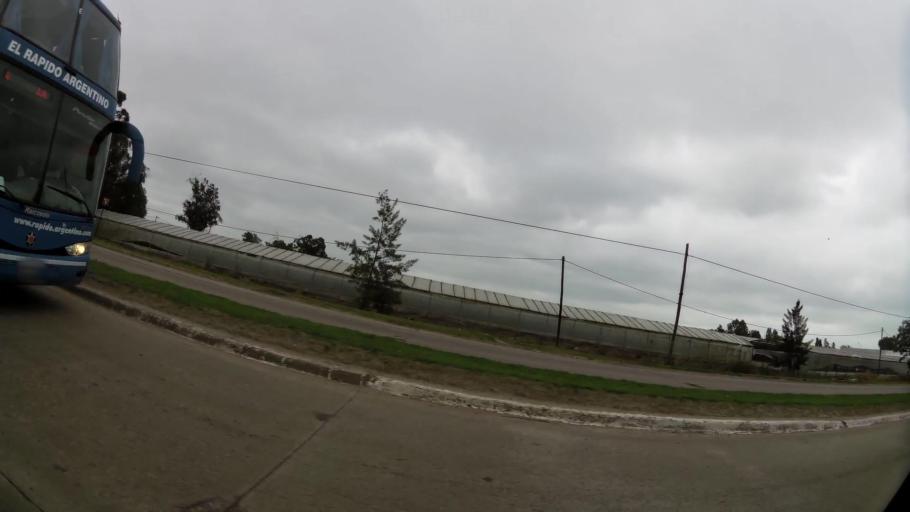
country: AR
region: Buenos Aires
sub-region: Partido de La Plata
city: La Plata
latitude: -35.0199
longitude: -58.0751
